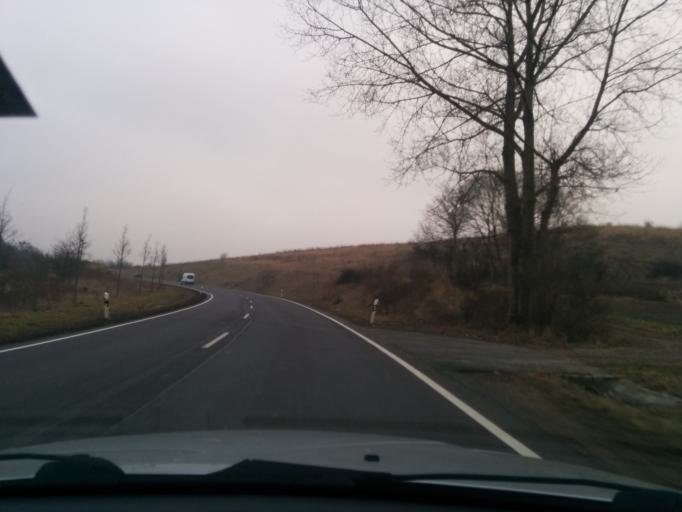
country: DE
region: Thuringia
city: Krauthausen
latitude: 51.0167
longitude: 10.2600
